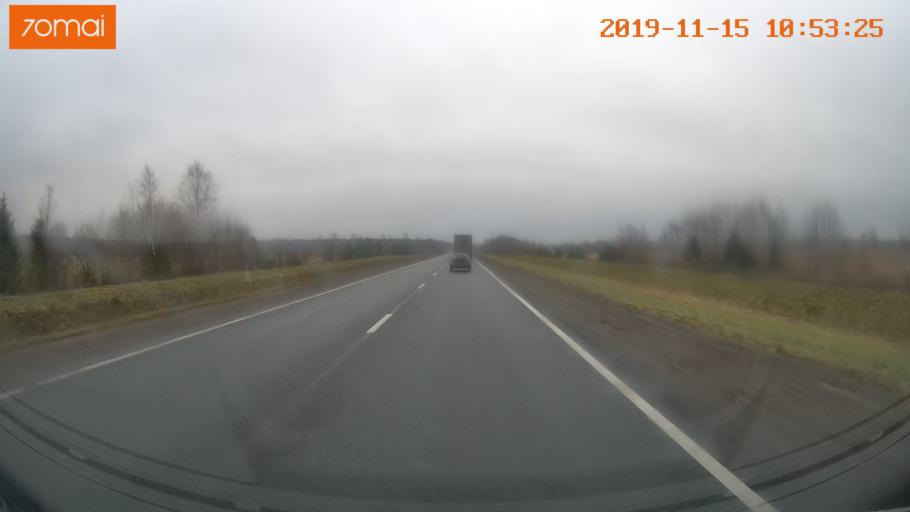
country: RU
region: Vologda
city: Chebsara
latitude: 59.1694
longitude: 38.7539
